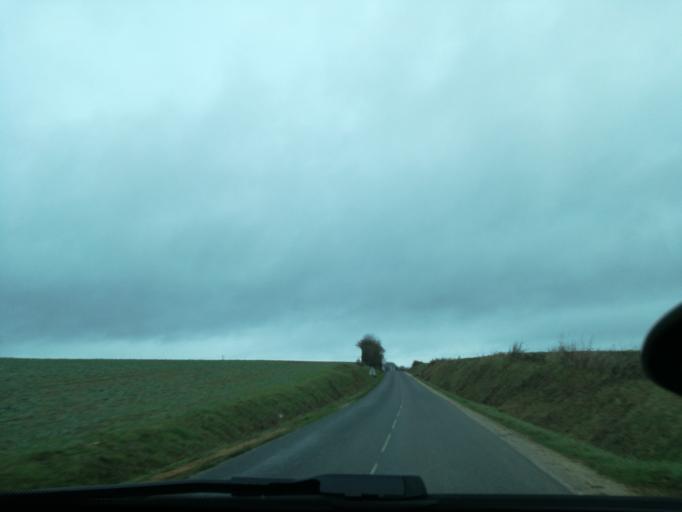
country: FR
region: Lorraine
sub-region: Departement de la Meuse
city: Revigny-sur-Ornain
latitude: 48.8804
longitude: 5.0799
